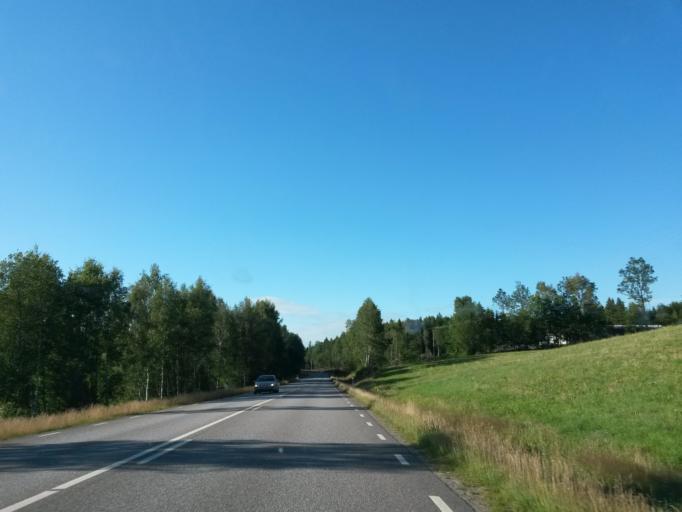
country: SE
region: Vaestra Goetaland
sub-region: Vargarda Kommun
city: Vargarda
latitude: 57.9620
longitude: 12.8139
